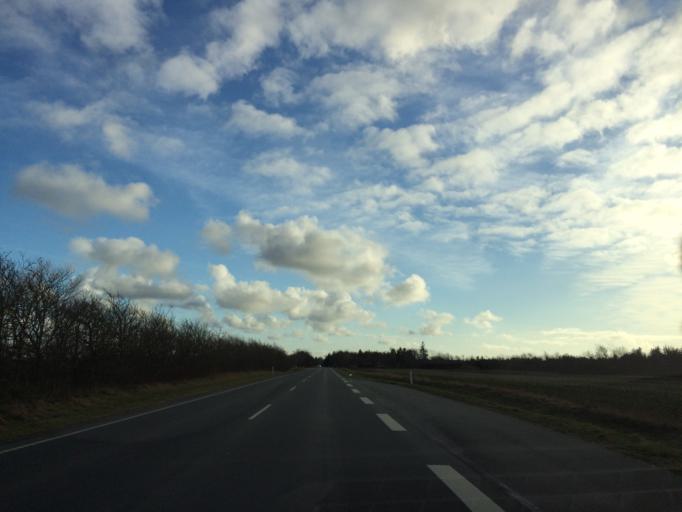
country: DK
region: Central Jutland
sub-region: Holstebro Kommune
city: Ulfborg
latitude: 56.3594
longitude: 8.3368
